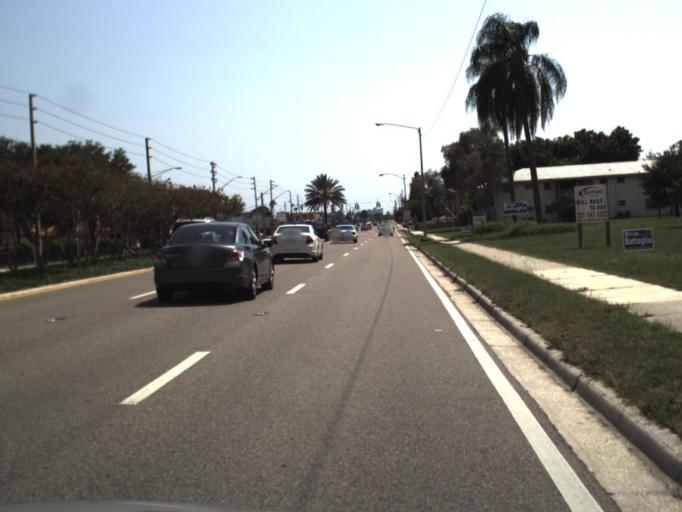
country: US
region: Florida
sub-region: Pinellas County
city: South Pasadena
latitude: 27.7646
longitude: -82.7343
